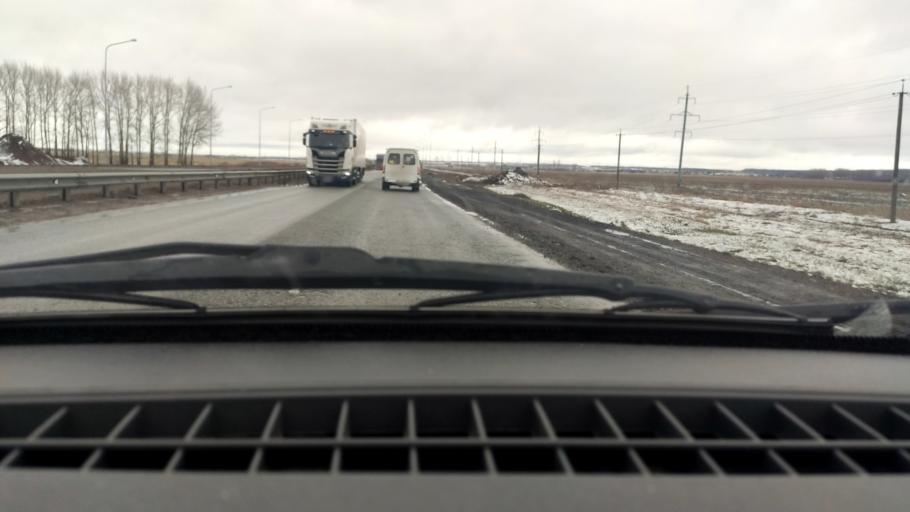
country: RU
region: Bashkortostan
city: Asanovo
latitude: 54.8838
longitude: 55.6870
